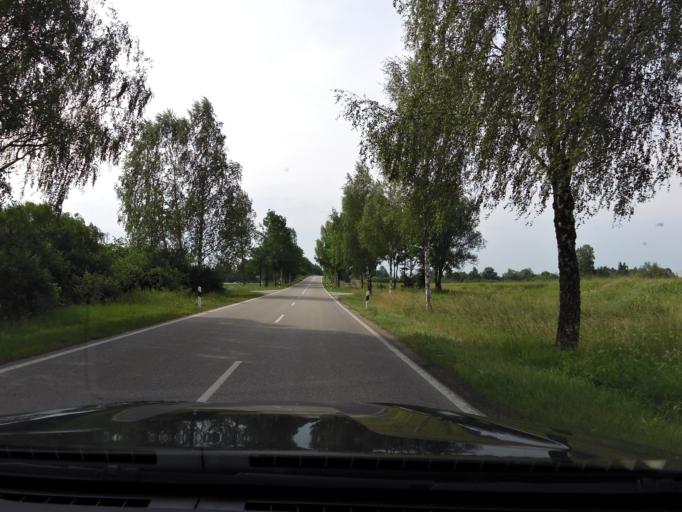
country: DE
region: Bavaria
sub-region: Upper Bavaria
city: Langenpreising
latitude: 48.4294
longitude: 11.9355
